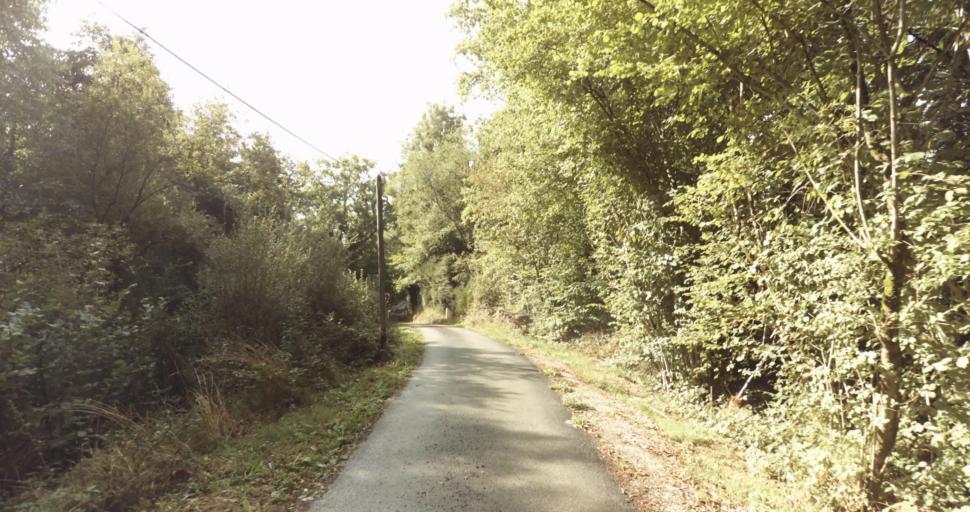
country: FR
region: Lower Normandy
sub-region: Departement de l'Orne
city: Sainte-Gauburge-Sainte-Colombe
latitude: 48.6854
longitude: 0.3833
